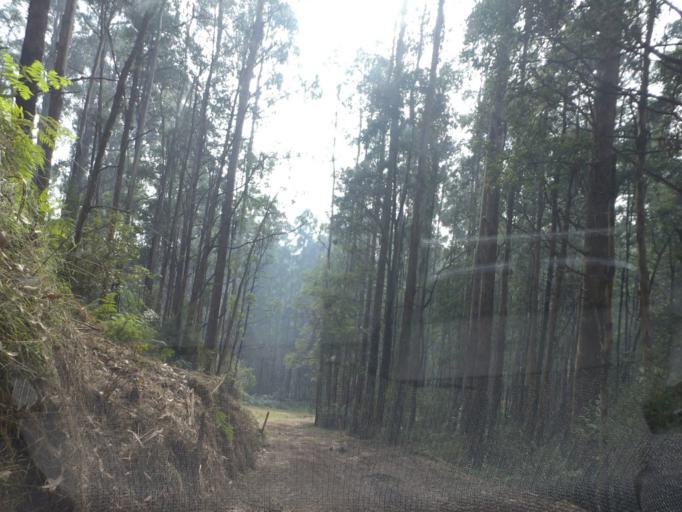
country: AU
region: Victoria
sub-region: Yarra Ranges
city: Healesville
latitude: -37.5715
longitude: 145.5795
